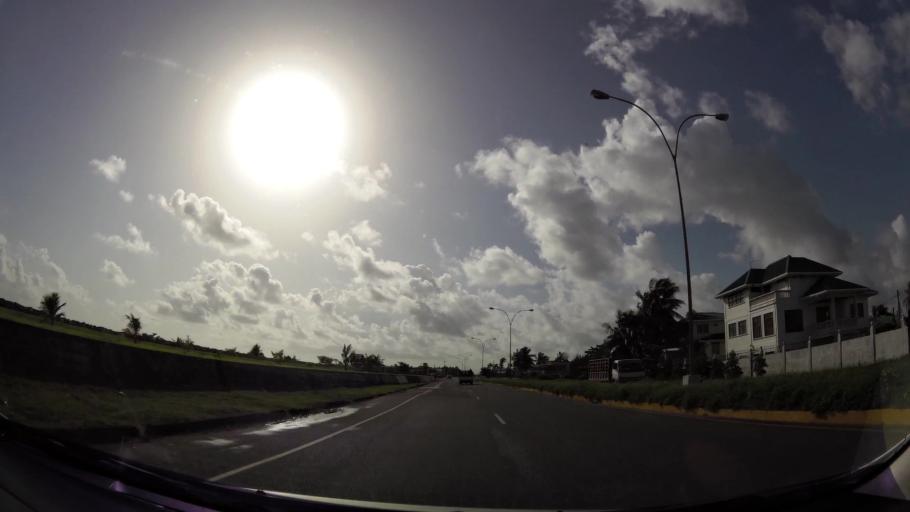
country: GY
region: Demerara-Mahaica
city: Georgetown
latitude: 6.8226
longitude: -58.1025
